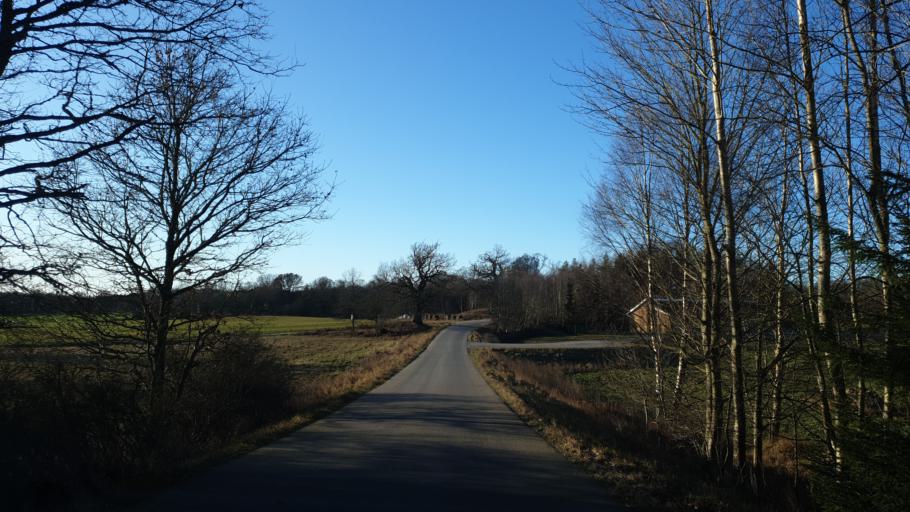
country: SE
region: Blekinge
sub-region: Karlskrona Kommun
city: Nattraby
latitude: 56.2624
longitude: 15.4333
